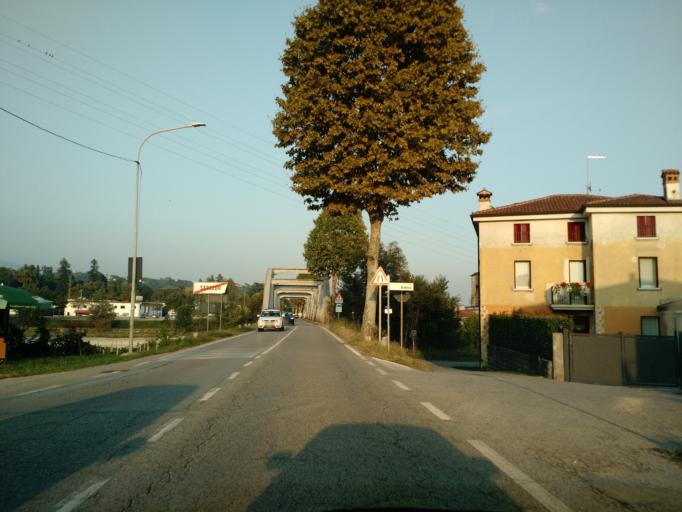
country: IT
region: Veneto
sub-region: Provincia di Vicenza
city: Sarcedo
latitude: 45.7049
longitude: 11.5428
